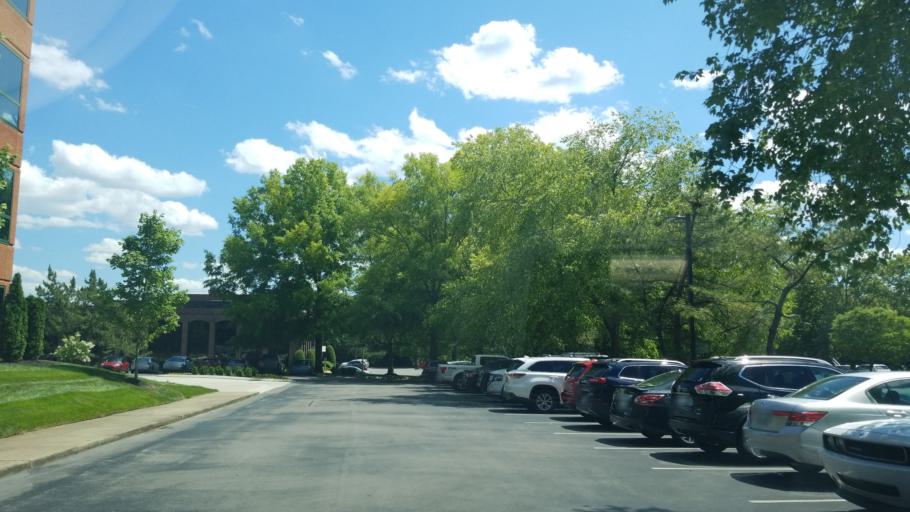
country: US
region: Tennessee
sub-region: Williamson County
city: Brentwood
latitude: 36.0378
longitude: -86.8077
